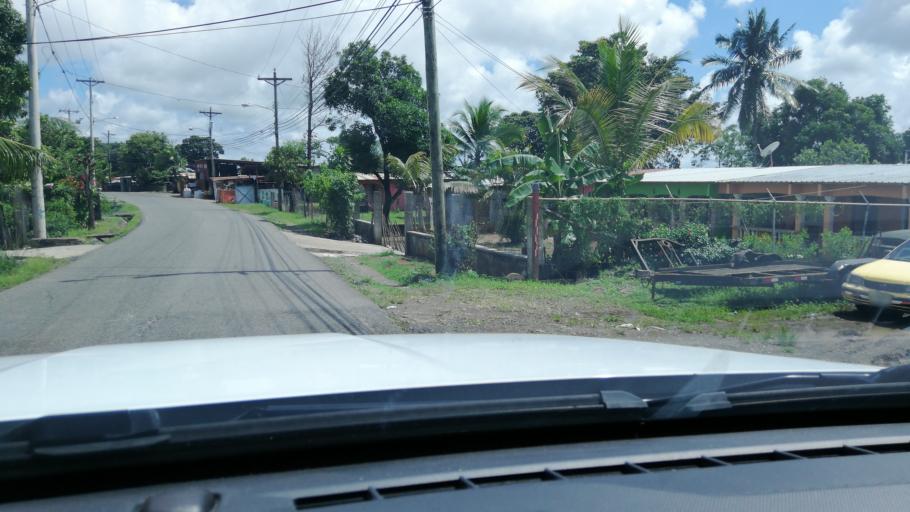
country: PA
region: Panama
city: Cabra Numero Uno
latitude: 9.1099
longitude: -79.3427
